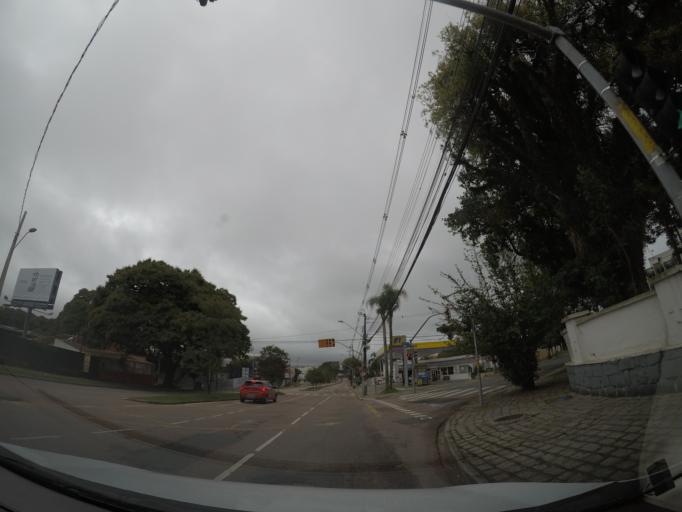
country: BR
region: Parana
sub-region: Curitiba
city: Curitiba
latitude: -25.4494
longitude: -49.3007
